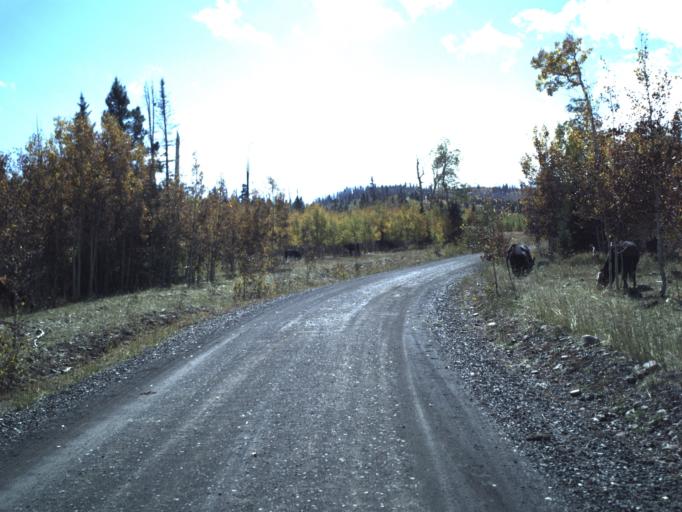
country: US
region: Utah
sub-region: Piute County
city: Junction
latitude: 38.2517
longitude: -112.3364
